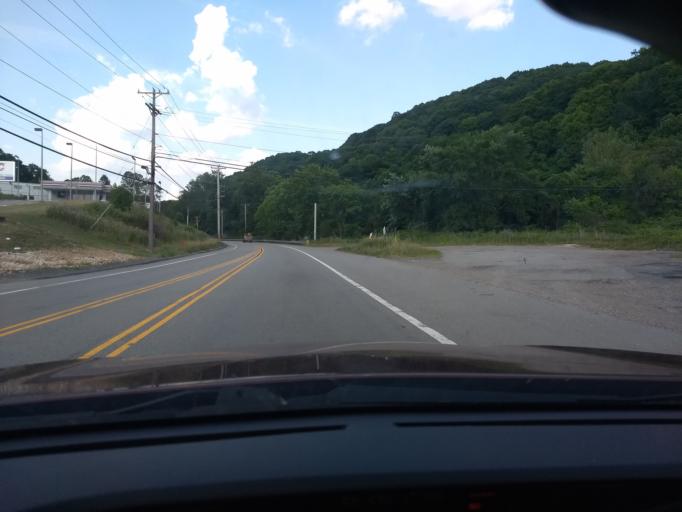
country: US
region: Pennsylvania
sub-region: Allegheny County
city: White Oak
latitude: 40.3384
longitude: -79.8057
